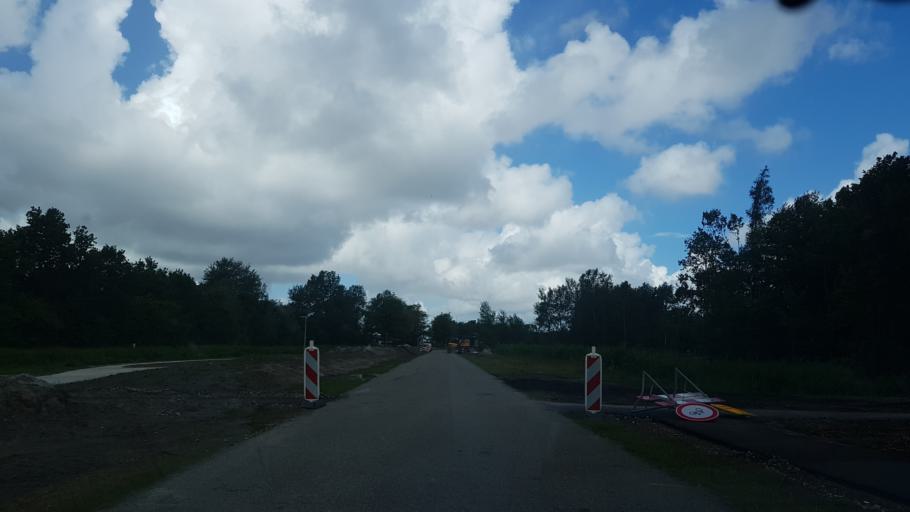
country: NL
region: Friesland
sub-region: Gemeente Dongeradeel
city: Anjum
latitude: 53.4028
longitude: 6.2166
